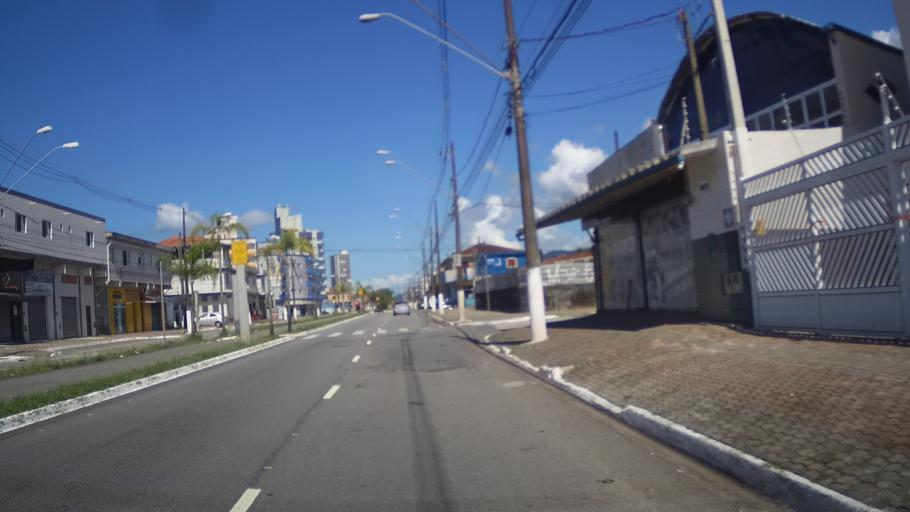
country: BR
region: Sao Paulo
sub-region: Mongagua
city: Mongagua
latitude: -24.0424
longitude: -46.5200
